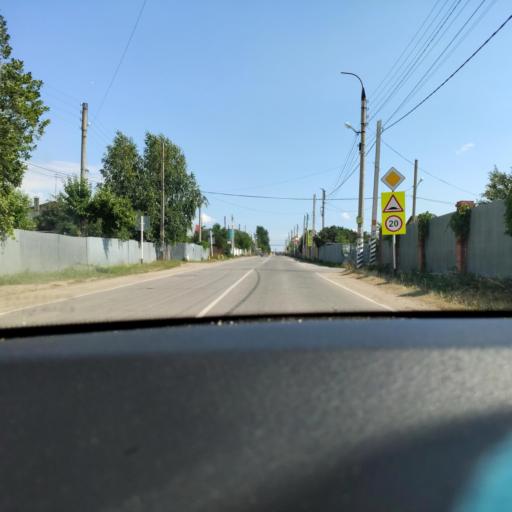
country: RU
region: Samara
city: Volzhskiy
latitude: 53.4516
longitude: 50.1730
